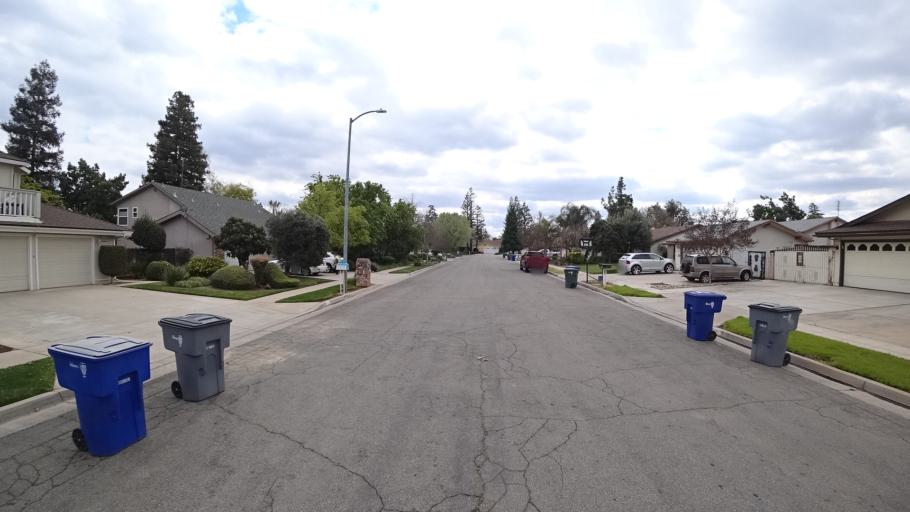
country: US
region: California
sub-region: Fresno County
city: Fresno
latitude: 36.8351
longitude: -119.8034
